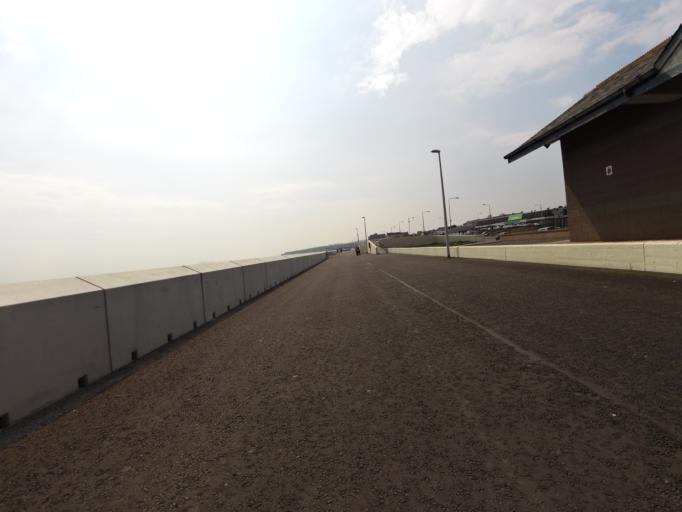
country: GB
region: Scotland
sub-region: Fife
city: Kirkcaldy
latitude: 56.1077
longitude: -3.1571
